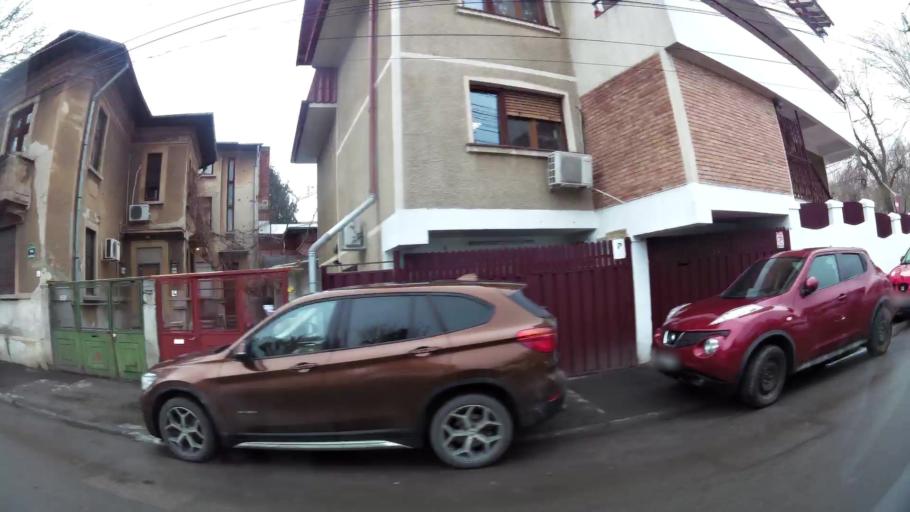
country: RO
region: Bucuresti
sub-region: Municipiul Bucuresti
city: Bucuresti
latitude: 44.4589
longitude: 26.0640
